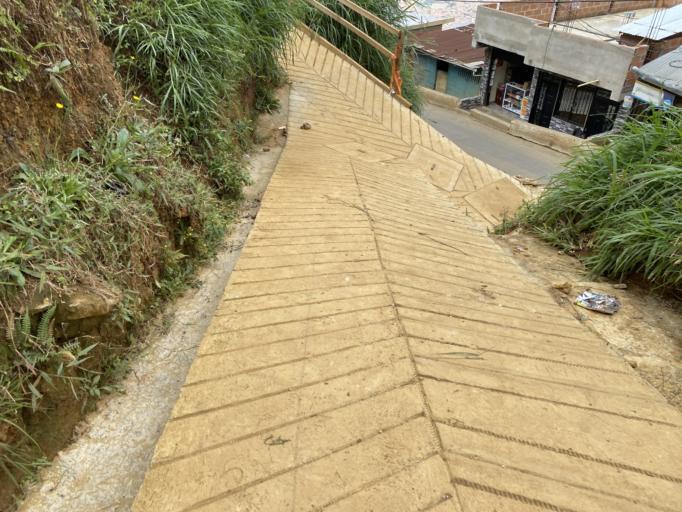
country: CO
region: Antioquia
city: Medellin
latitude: 6.2668
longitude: -75.5396
